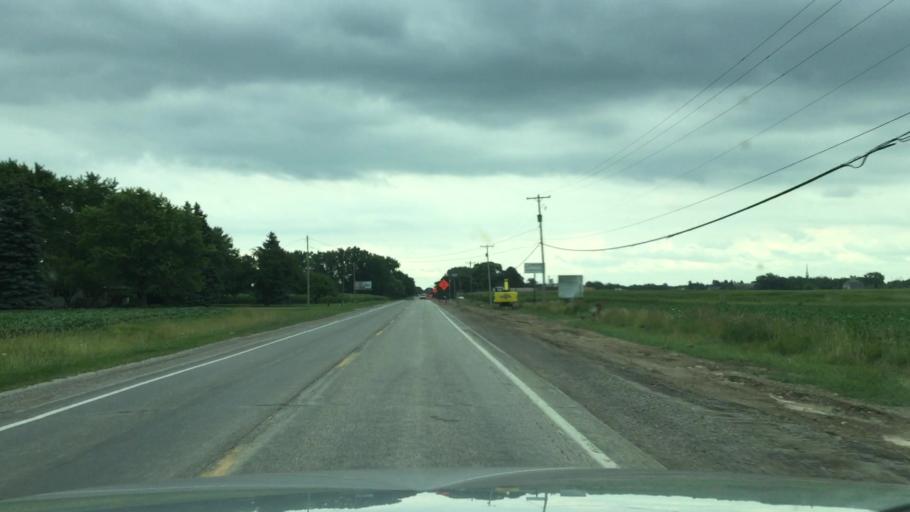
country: US
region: Michigan
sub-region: Saginaw County
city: Frankenmuth
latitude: 43.3358
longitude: -83.7762
